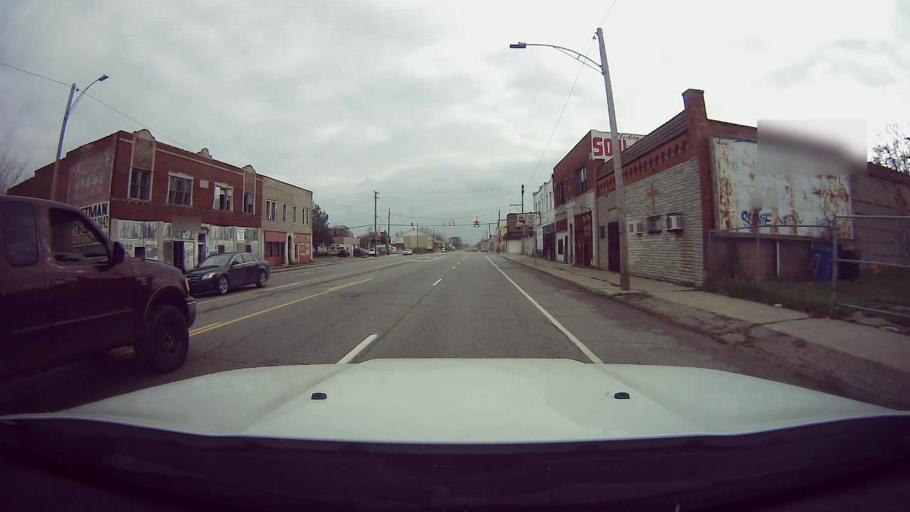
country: US
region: Michigan
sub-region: Wayne County
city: Highland Park
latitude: 42.3908
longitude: -83.1206
